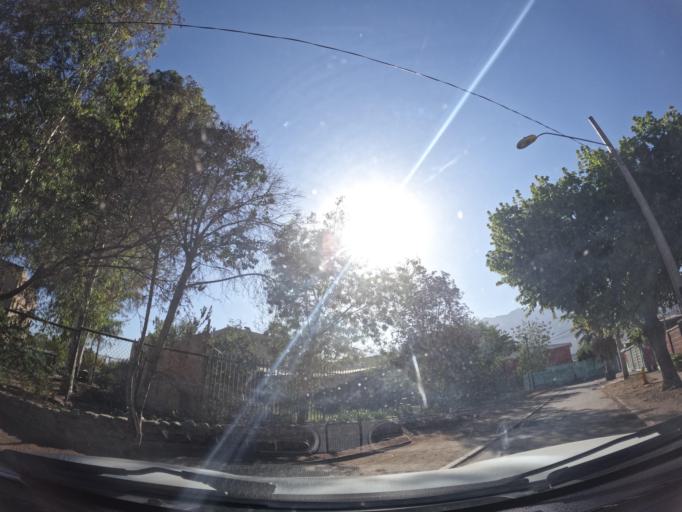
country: CL
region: Santiago Metropolitan
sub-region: Provincia de Santiago
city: Villa Presidente Frei, Nunoa, Santiago, Chile
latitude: -33.4636
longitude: -70.5551
